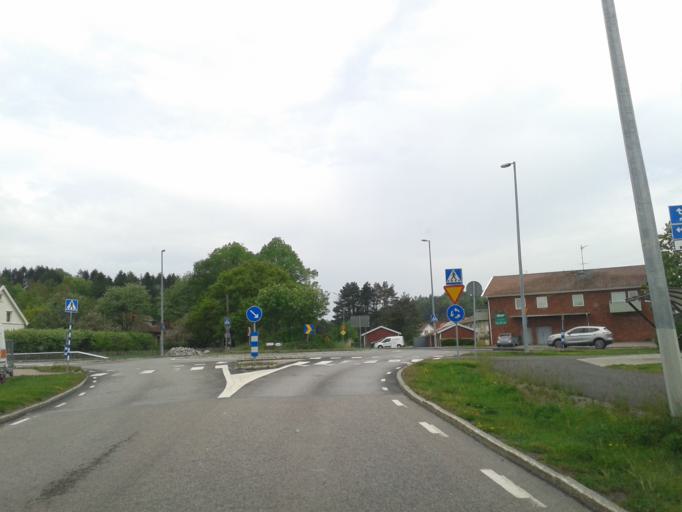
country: SE
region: Vaestra Goetaland
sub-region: Kungalvs Kommun
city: Kode
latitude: 57.8436
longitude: 11.7919
